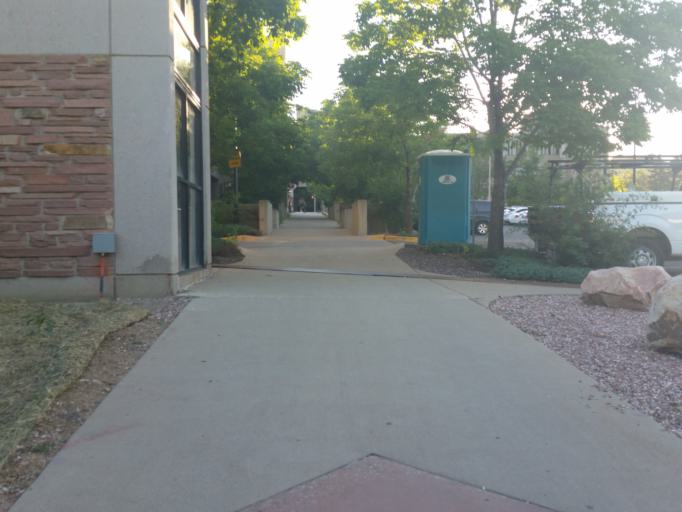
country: US
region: Colorado
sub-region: Boulder County
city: Boulder
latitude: 40.0073
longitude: -105.2600
